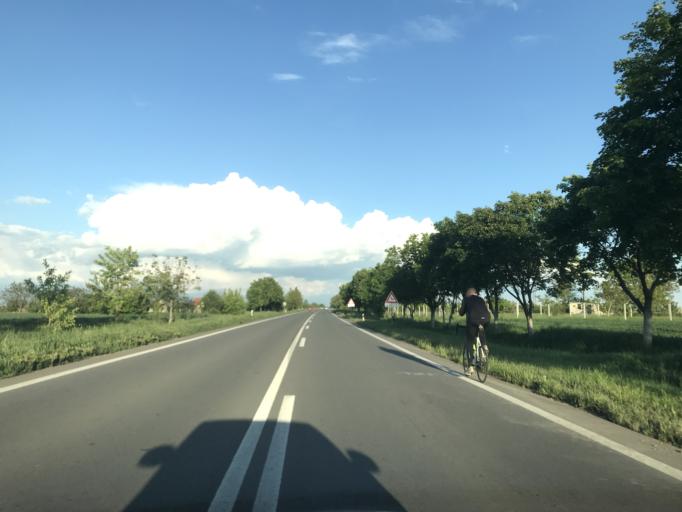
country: RS
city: Aradac
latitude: 45.3912
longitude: 20.3011
